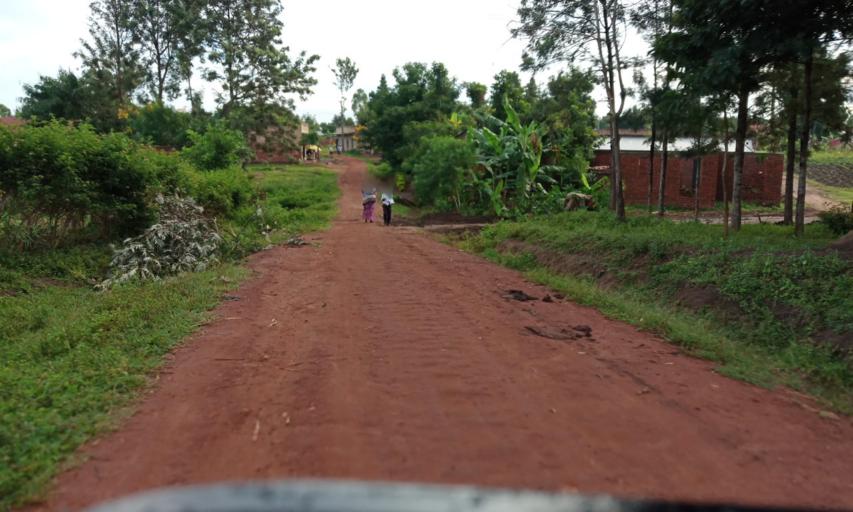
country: UG
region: Eastern Region
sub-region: Mbale District
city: Mbale
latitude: 1.1458
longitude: 34.1677
